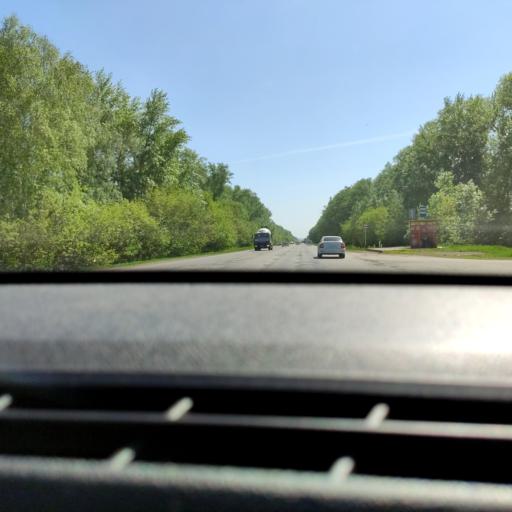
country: RU
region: Samara
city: Tol'yatti
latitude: 53.6315
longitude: 49.4175
